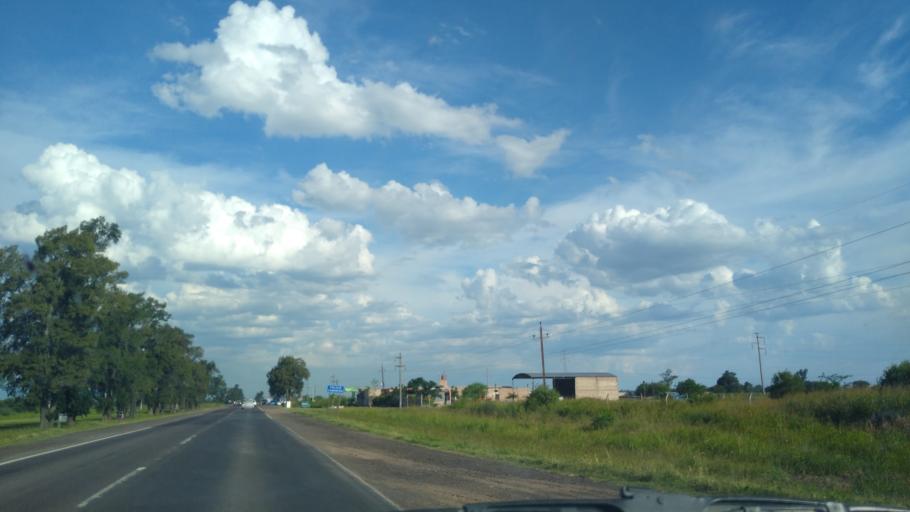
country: AR
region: Chaco
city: Presidencia Roque Saenz Pena
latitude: -26.8163
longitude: -60.4077
